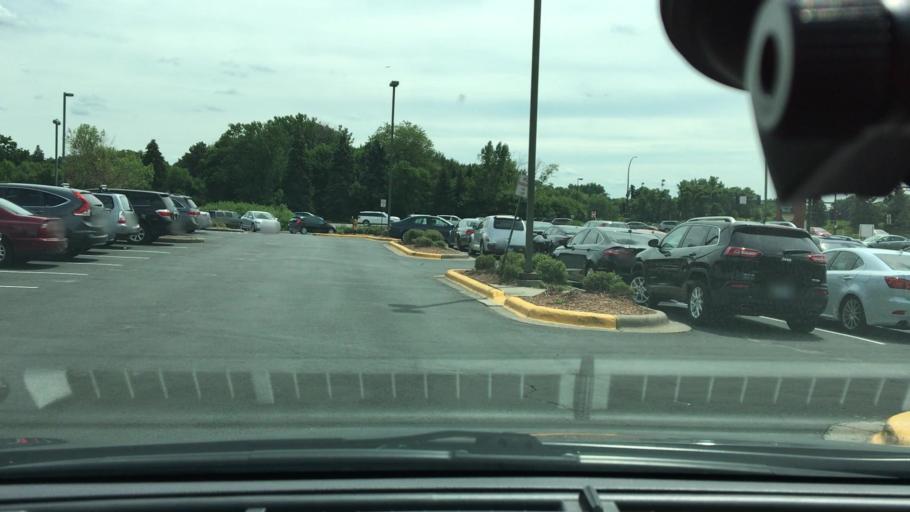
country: US
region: Minnesota
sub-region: Hennepin County
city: Golden Valley
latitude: 44.9848
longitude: -93.3794
